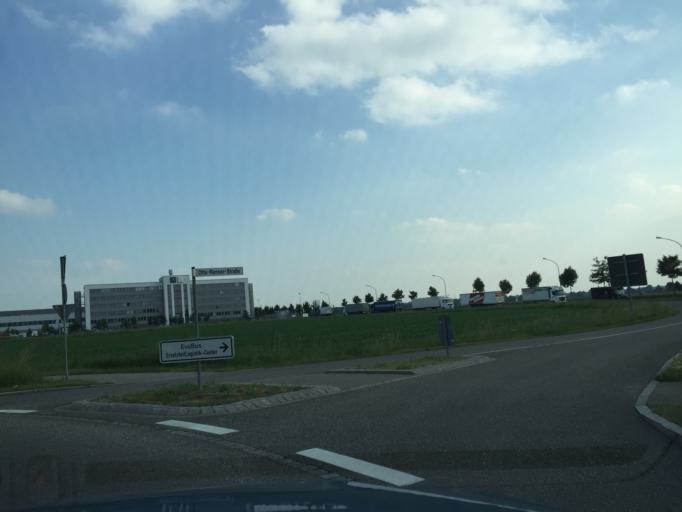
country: DE
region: Bavaria
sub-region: Swabia
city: Neu-Ulm
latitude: 48.3788
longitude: 10.0308
